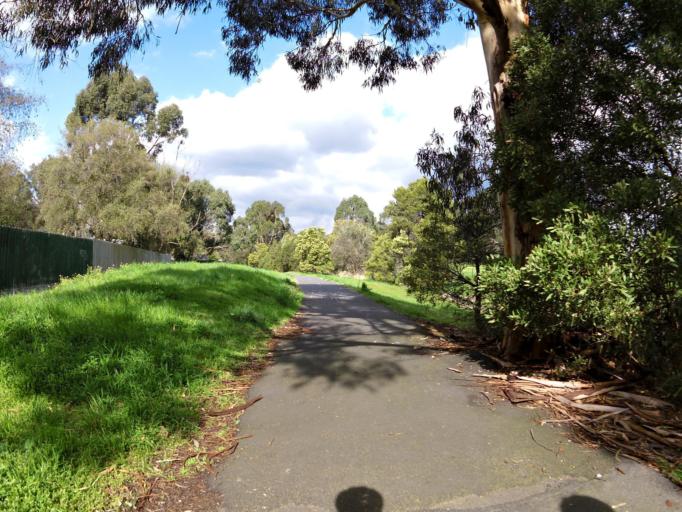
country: AU
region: Victoria
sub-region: Maroondah
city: Bayswater North
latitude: -37.8356
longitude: 145.2971
